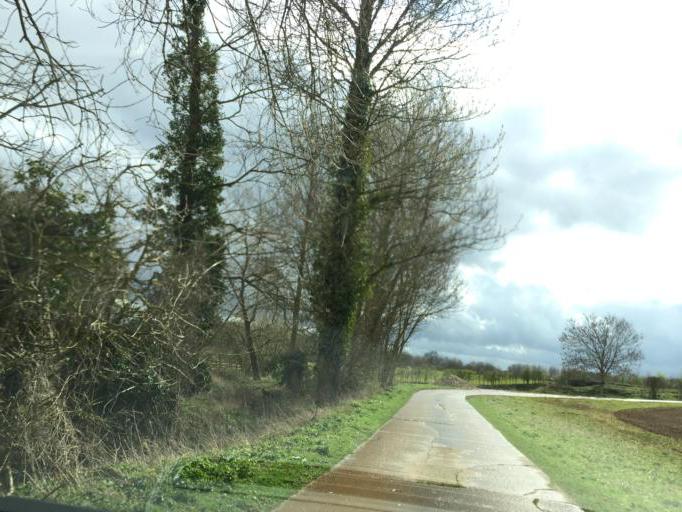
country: GB
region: England
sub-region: Oxfordshire
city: Woodstock
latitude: 51.9008
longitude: -1.3815
